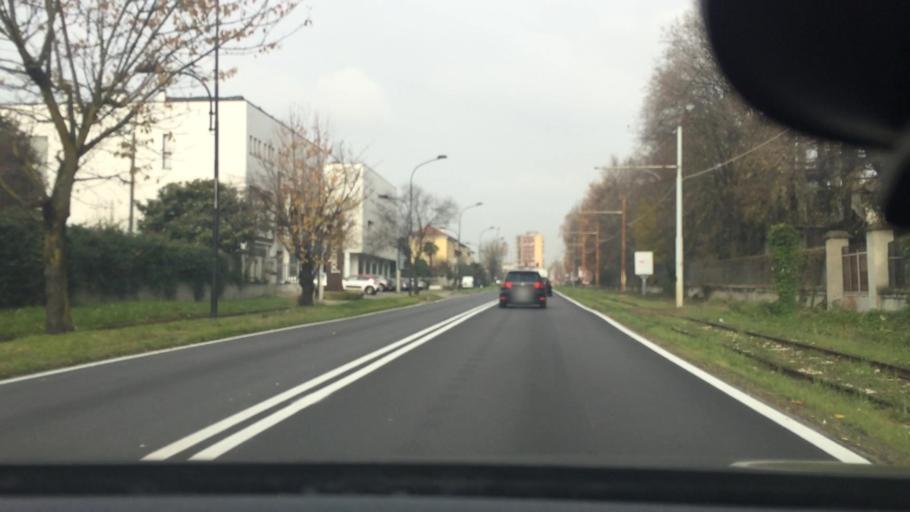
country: IT
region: Lombardy
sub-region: Provincia di Monza e Brianza
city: Limbiate
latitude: 45.6120
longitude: 9.1211
